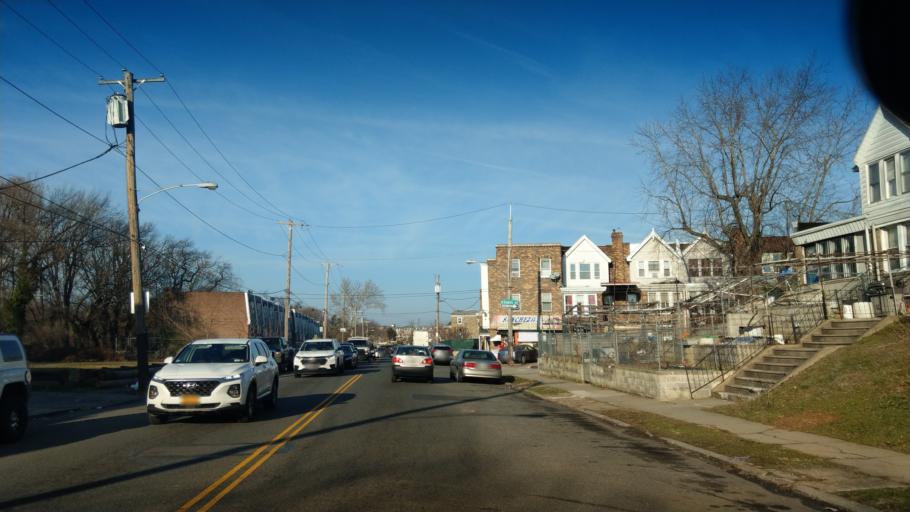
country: US
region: Pennsylvania
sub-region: Montgomery County
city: Rockledge
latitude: 40.0294
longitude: -75.1099
